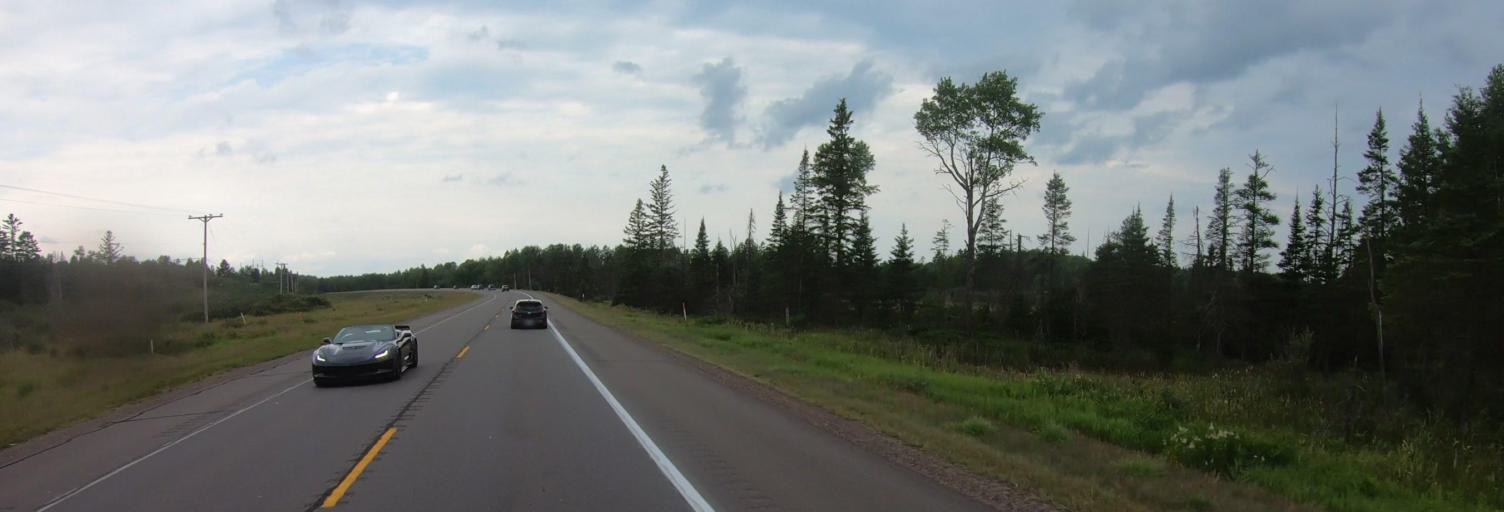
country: US
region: Michigan
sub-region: Marquette County
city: West Ishpeming
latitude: 46.4958
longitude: -87.8768
